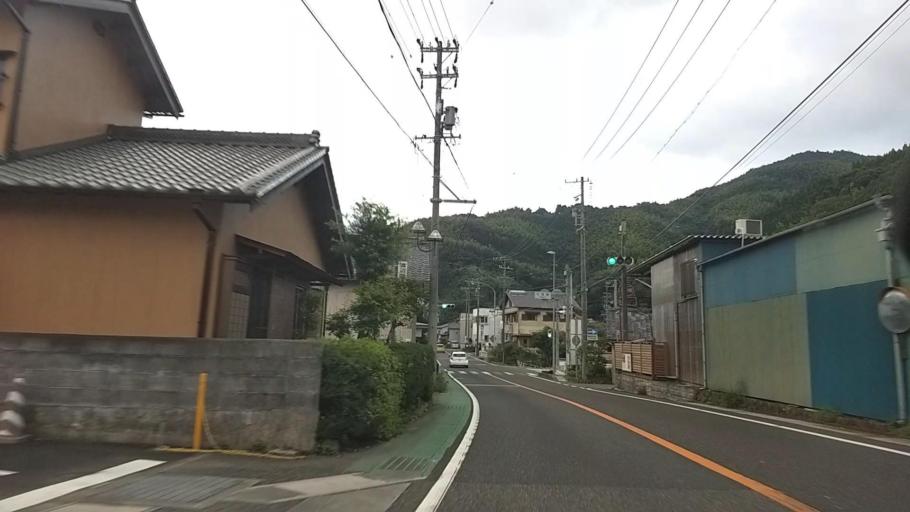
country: JP
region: Shizuoka
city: Fujinomiya
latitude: 35.0847
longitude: 138.5141
